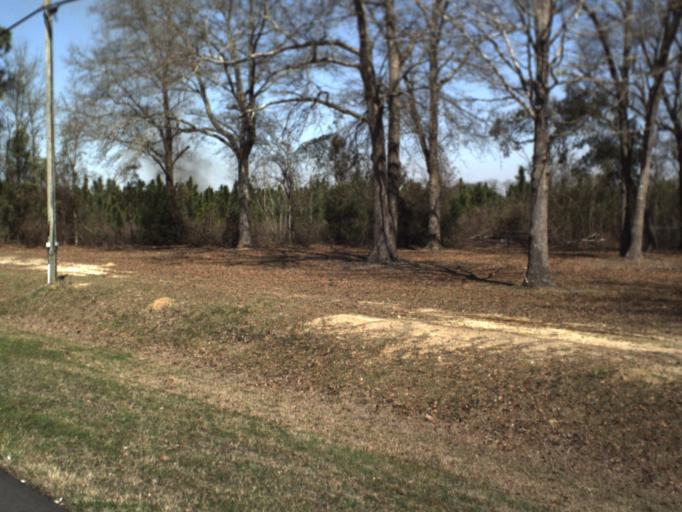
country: US
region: Florida
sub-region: Jackson County
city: Sneads
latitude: 30.8071
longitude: -85.0365
